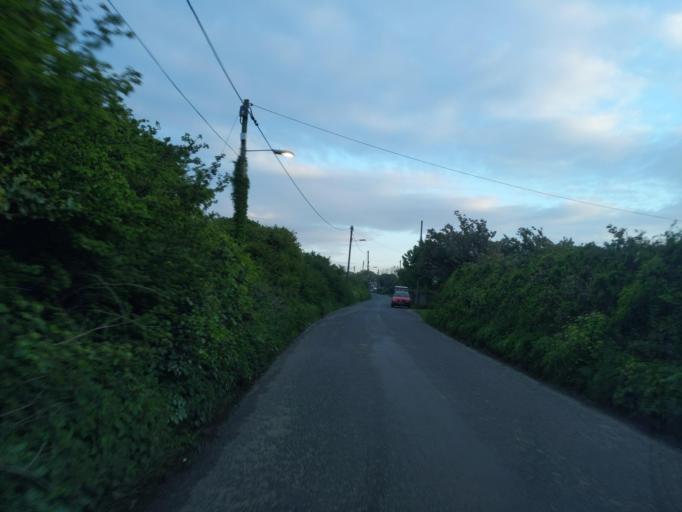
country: GB
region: England
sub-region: Cornwall
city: Polzeath
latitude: 50.5612
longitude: -4.8724
